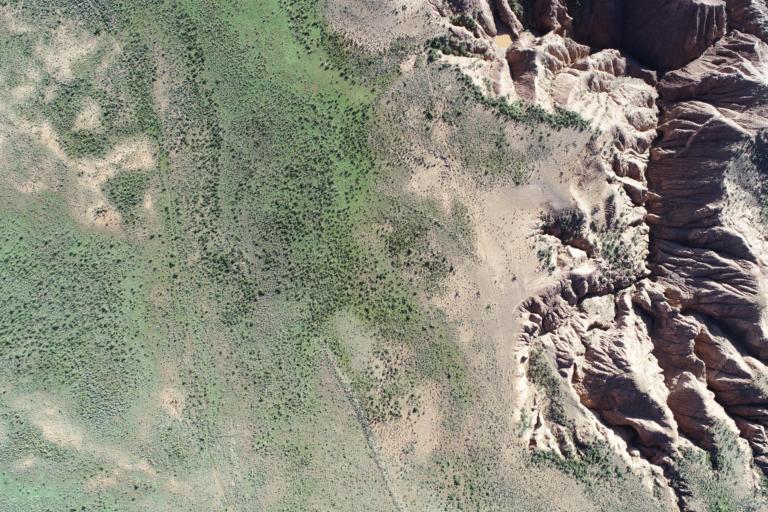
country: BO
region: La Paz
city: Curahuara de Carangas
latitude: -17.3041
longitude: -68.5005
